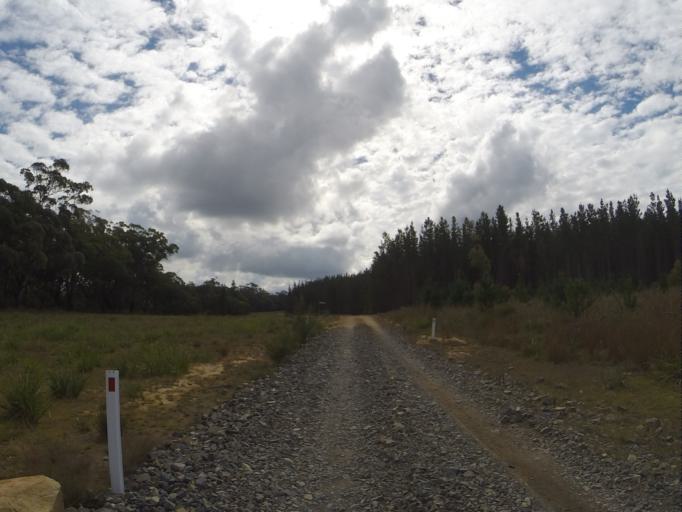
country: AU
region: New South Wales
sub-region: Wingecarribee
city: Moss Vale
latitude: -34.5173
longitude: 150.2275
